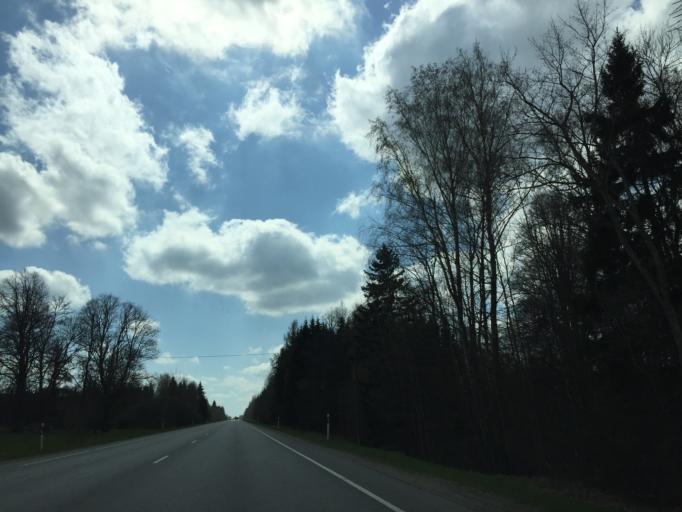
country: EE
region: Tartu
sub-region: Elva linn
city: Elva
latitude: 58.2119
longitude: 26.3624
